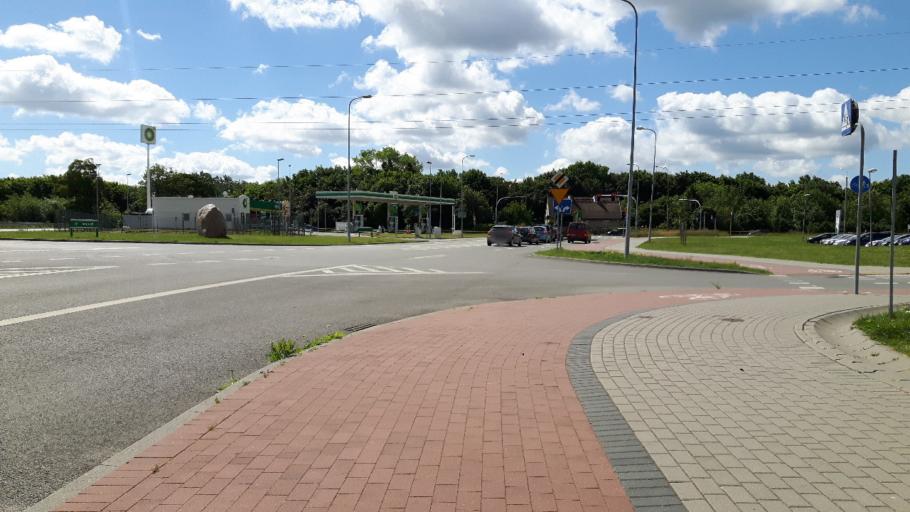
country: PL
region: Pomeranian Voivodeship
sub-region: Gdynia
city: Pogorze
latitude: 54.5649
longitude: 18.5060
